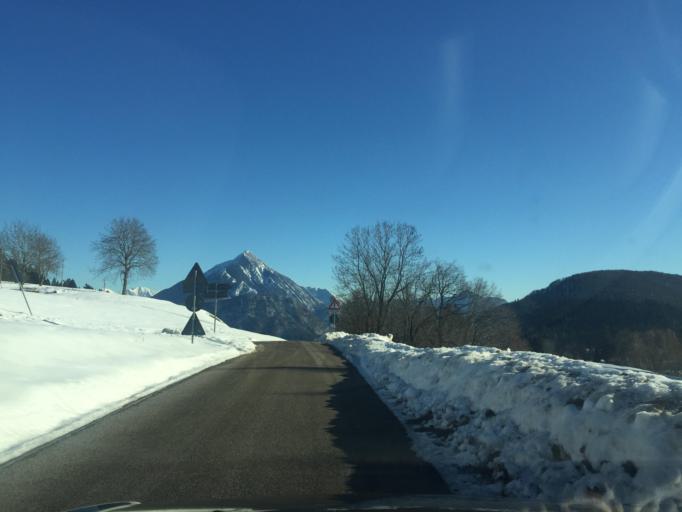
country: IT
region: Friuli Venezia Giulia
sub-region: Provincia di Udine
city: Lauco
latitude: 46.4311
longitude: 12.9716
